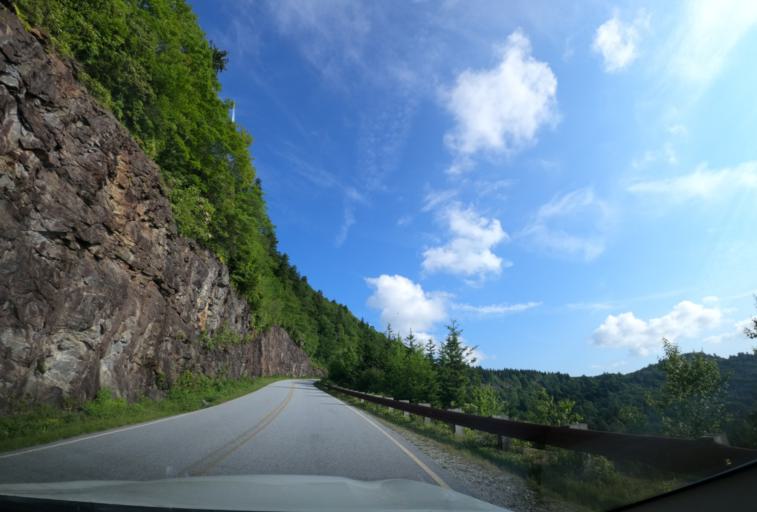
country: US
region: North Carolina
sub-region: Transylvania County
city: Brevard
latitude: 35.2920
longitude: -82.9144
